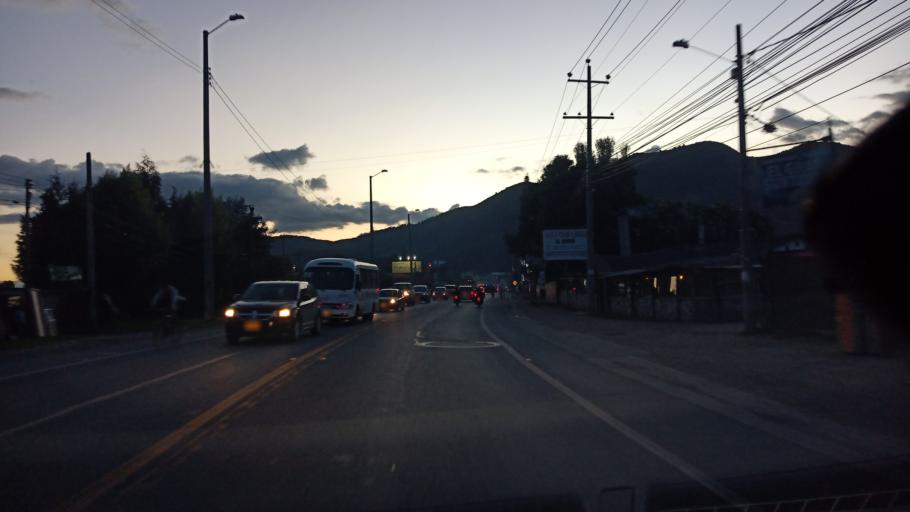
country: CO
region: Cundinamarca
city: Chia
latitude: 4.8500
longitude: -74.0740
